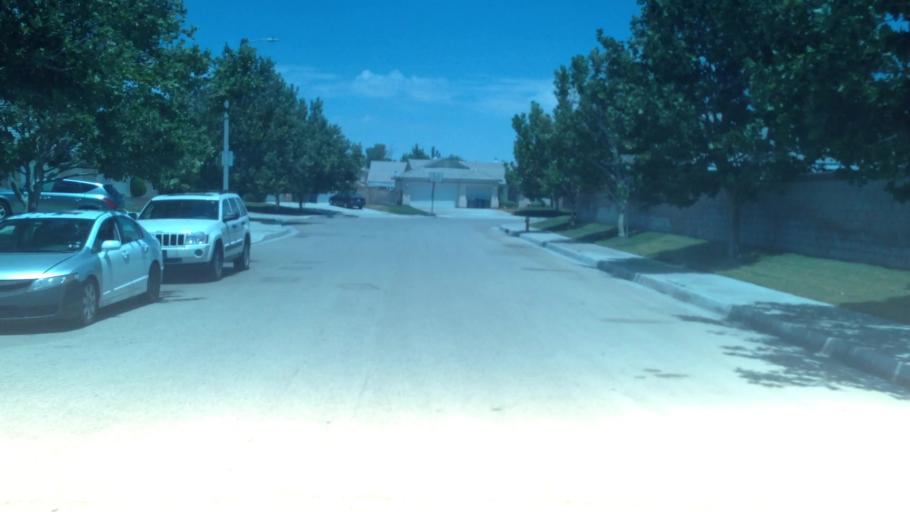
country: US
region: California
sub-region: Los Angeles County
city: Lancaster
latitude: 34.6843
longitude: -118.1707
